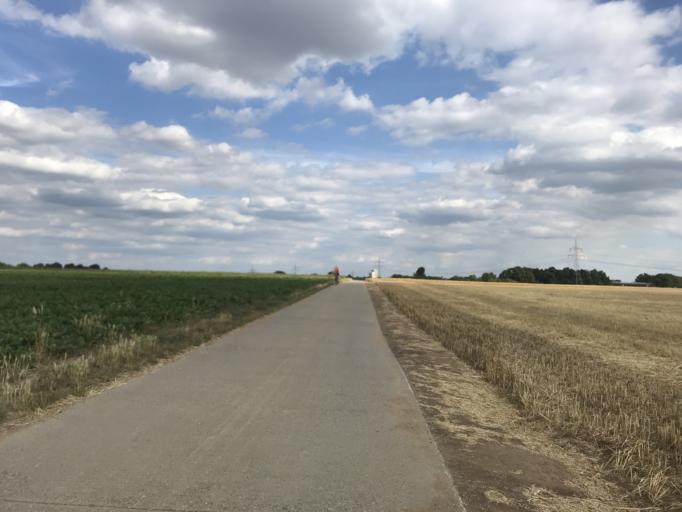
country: DE
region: Hesse
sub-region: Regierungsbezirk Darmstadt
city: Hochheim am Main
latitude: 50.0298
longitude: 8.3102
